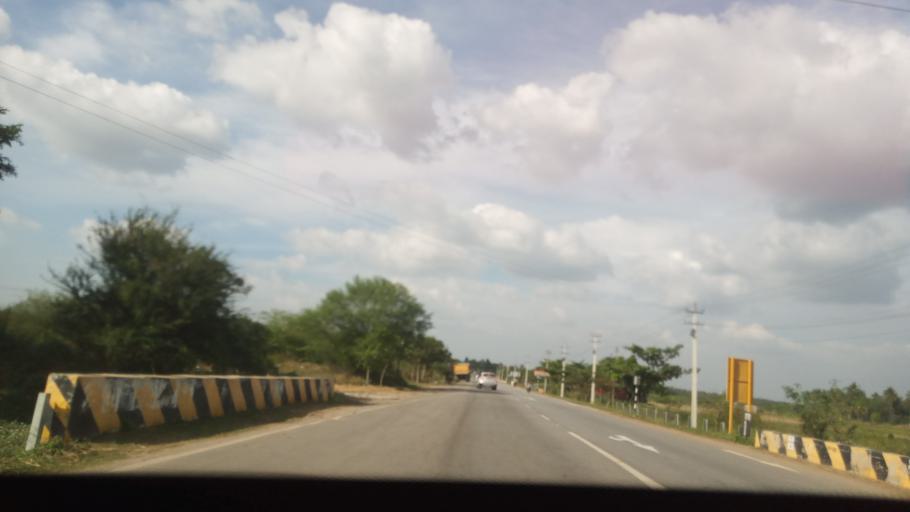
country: IN
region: Karnataka
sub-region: Mandya
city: Maddur
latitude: 12.6171
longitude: 77.0579
